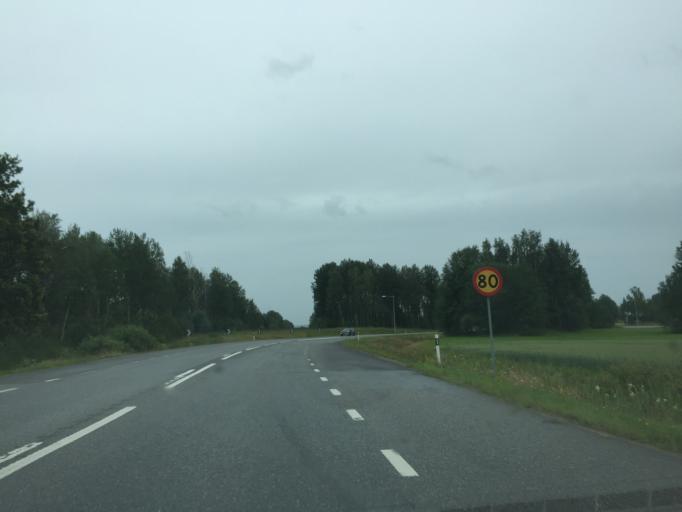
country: SE
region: OErebro
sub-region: Orebro Kommun
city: Orebro
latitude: 59.2073
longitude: 15.2364
